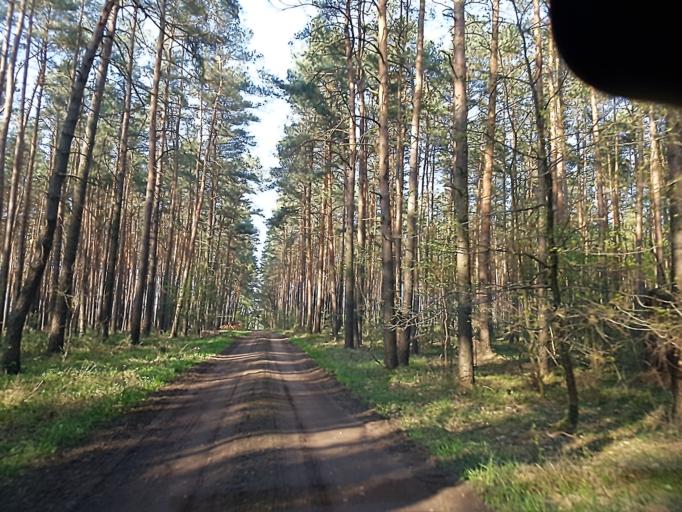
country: DE
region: Brandenburg
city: Schilda
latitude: 51.5600
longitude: 13.3821
